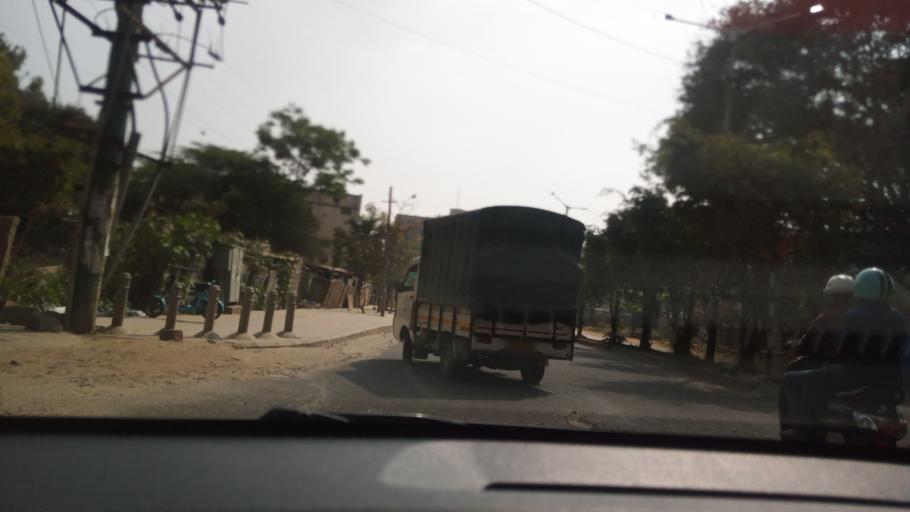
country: IN
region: Karnataka
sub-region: Bangalore Rural
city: Hoskote
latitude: 12.9920
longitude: 77.7136
